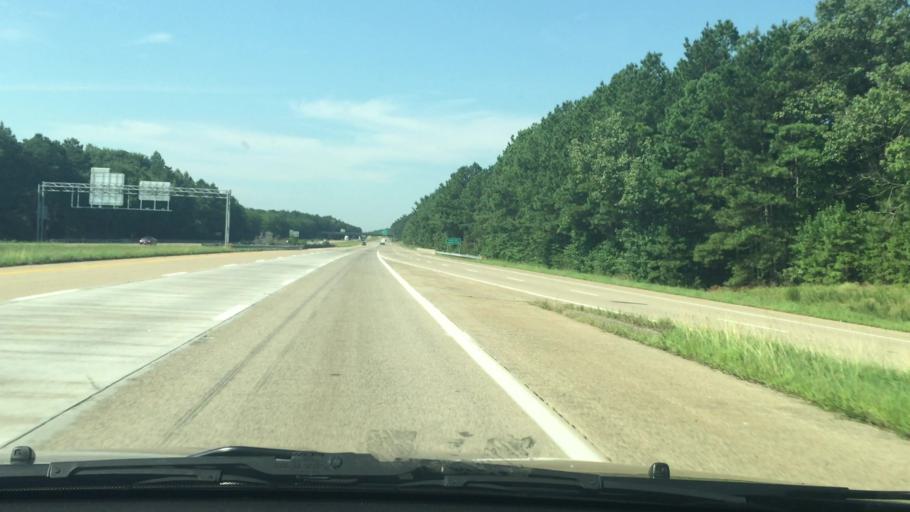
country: US
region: Virginia
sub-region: Henrico County
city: Sandston
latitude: 37.5028
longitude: -77.2819
